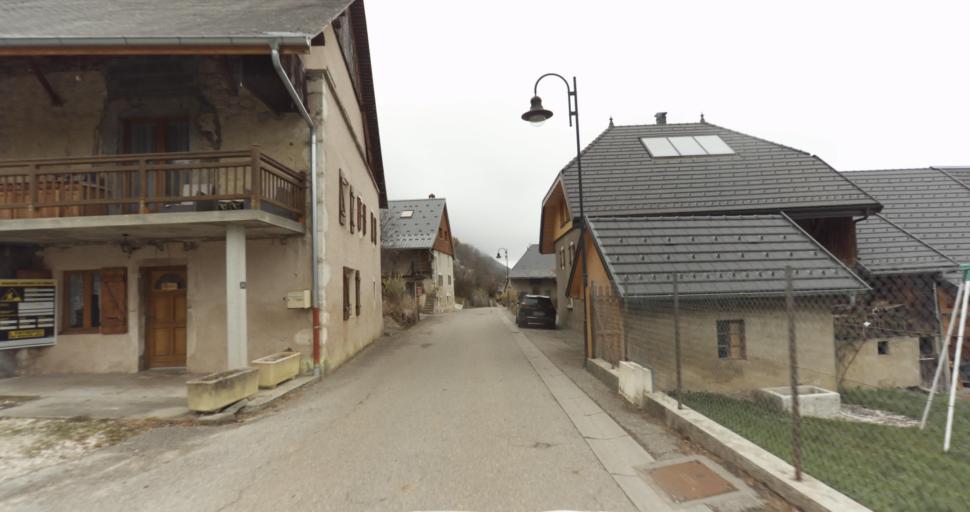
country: FR
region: Rhone-Alpes
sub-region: Departement de la Haute-Savoie
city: Doussard
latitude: 45.7945
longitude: 6.1888
